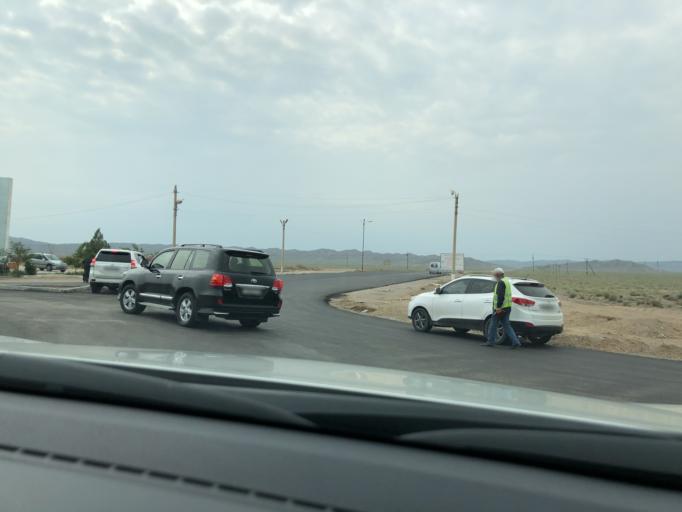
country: TJ
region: Viloyati Sughd
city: Kim
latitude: 40.1997
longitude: 70.4826
